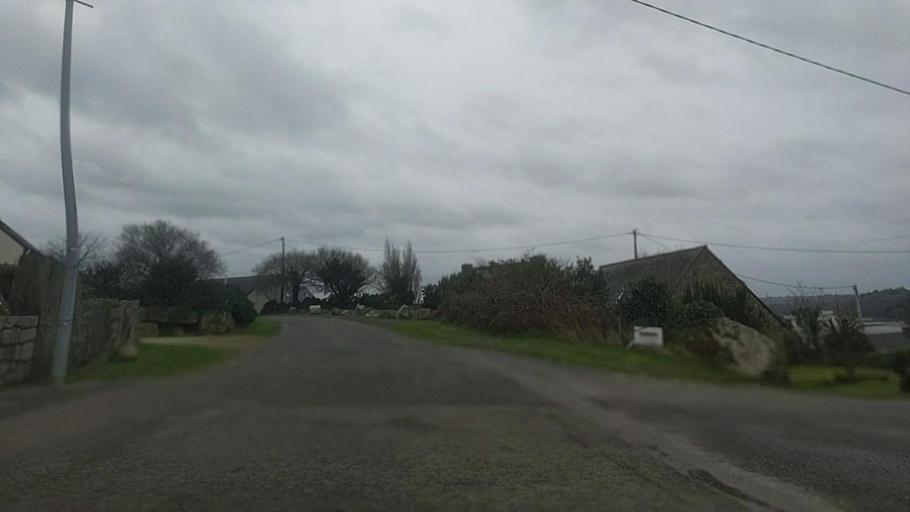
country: FR
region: Brittany
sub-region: Departement des Cotes-d'Armor
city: Tredarzec
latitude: 48.8215
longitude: -3.1942
